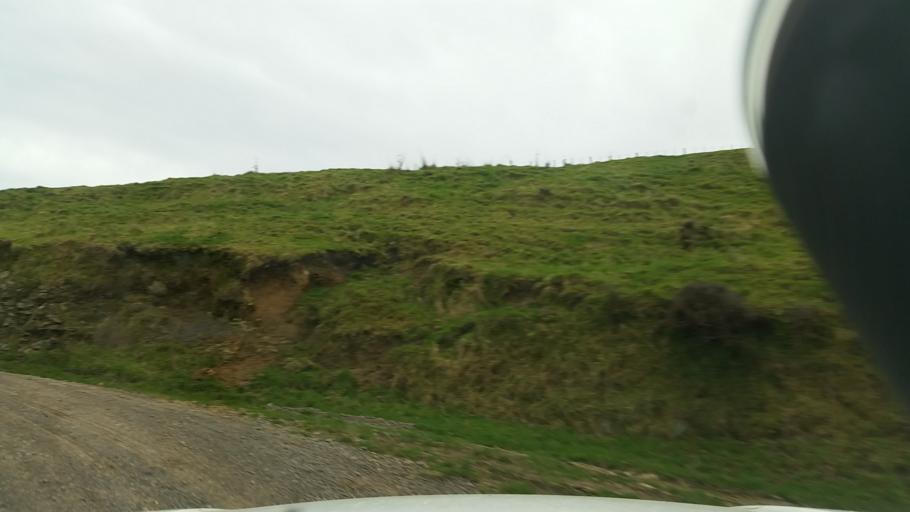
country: NZ
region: Canterbury
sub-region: Christchurch City
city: Christchurch
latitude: -43.8617
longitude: 173.0316
